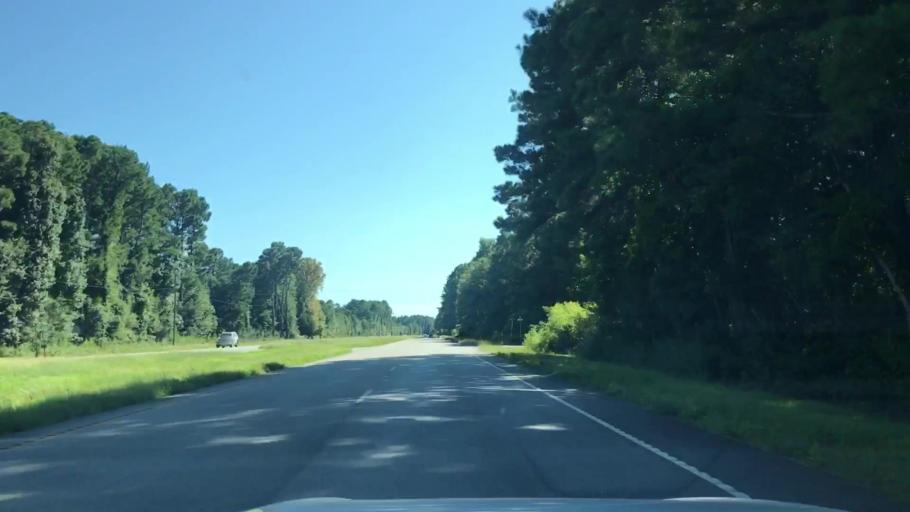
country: US
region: South Carolina
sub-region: Charleston County
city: Awendaw
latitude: 33.1097
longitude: -79.4613
